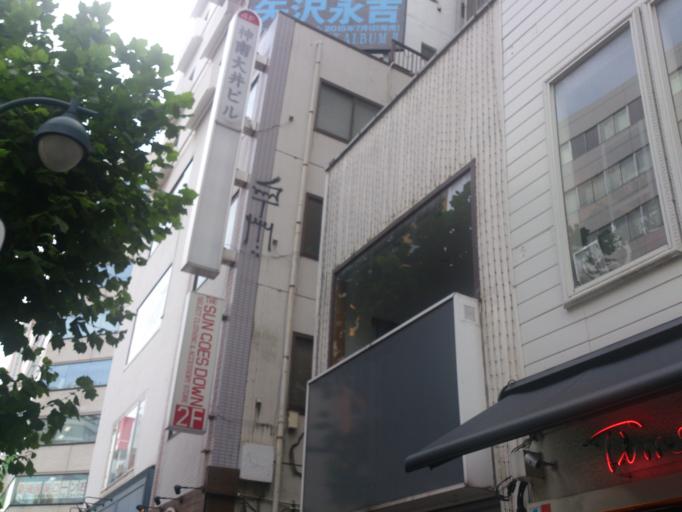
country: JP
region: Tokyo
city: Tokyo
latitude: 35.6625
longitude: 139.7009
